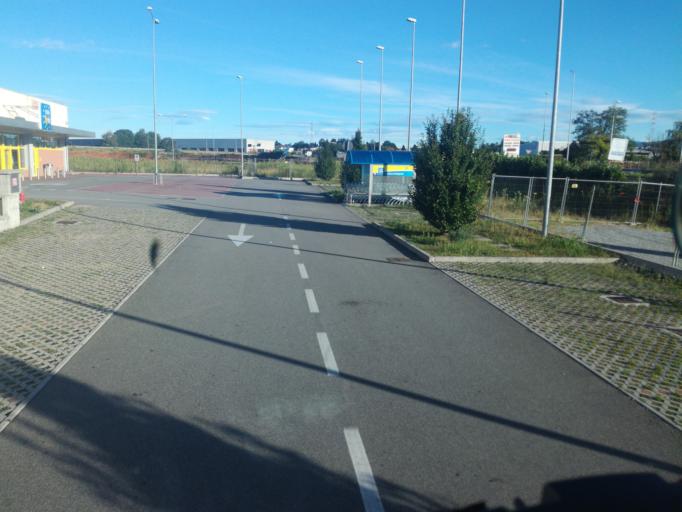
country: IT
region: Lombardy
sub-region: Provincia di Como
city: Carimate
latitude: 45.6925
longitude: 9.1023
